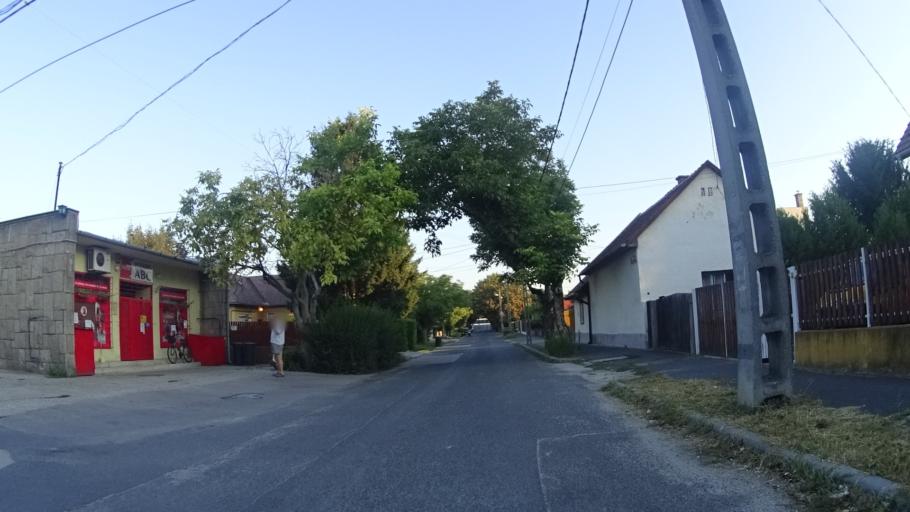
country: HU
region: Pest
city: Halasztelek
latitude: 47.3950
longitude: 19.0050
